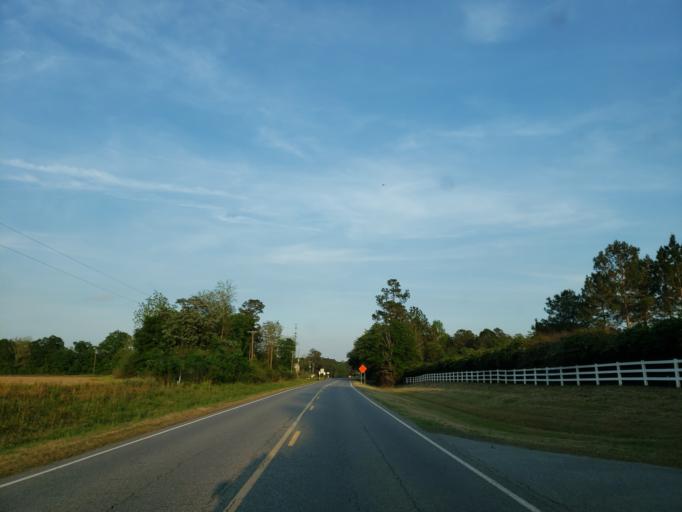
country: US
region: Georgia
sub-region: Lowndes County
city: Hahira
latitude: 30.9948
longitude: -83.4019
